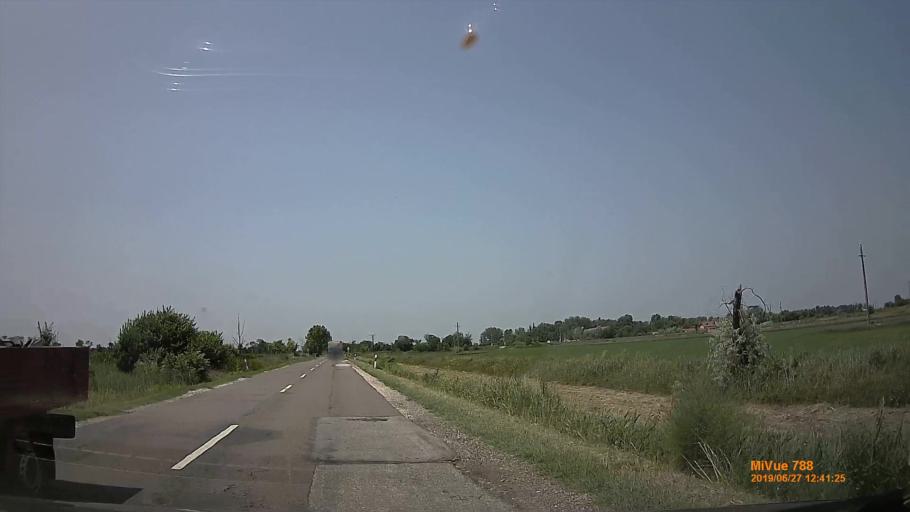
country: HU
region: Pest
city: Tortel
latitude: 47.1805
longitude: 19.8975
